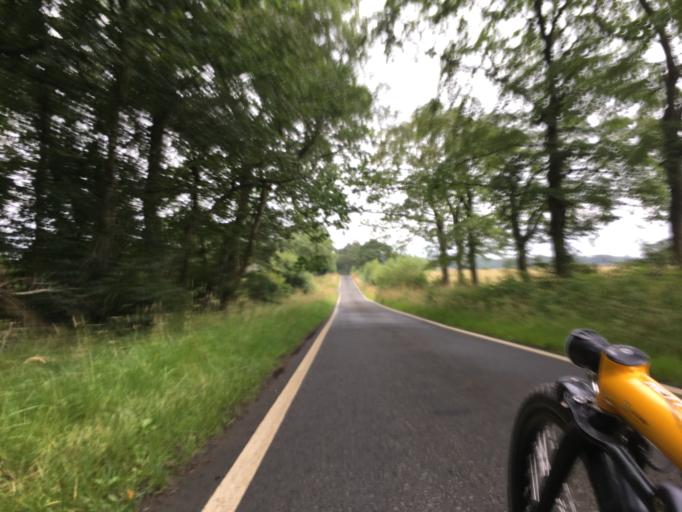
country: GB
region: Scotland
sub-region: West Lothian
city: West Calder
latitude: 55.8495
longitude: -3.5334
